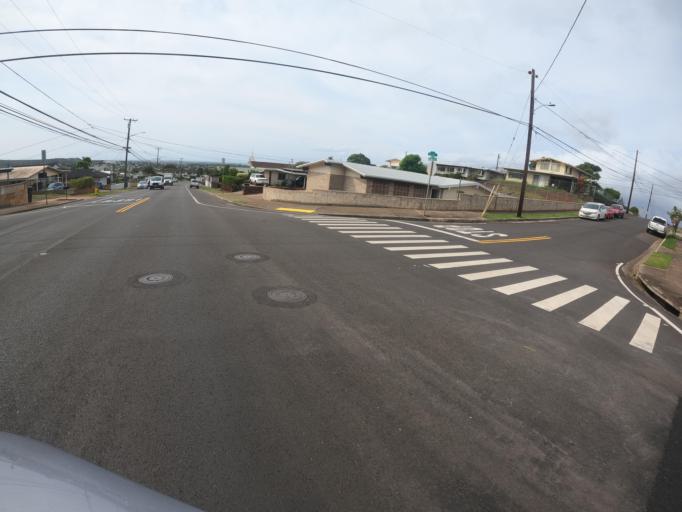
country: US
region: Hawaii
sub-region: Honolulu County
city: Halawa Heights
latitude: 21.3769
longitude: -157.9169
